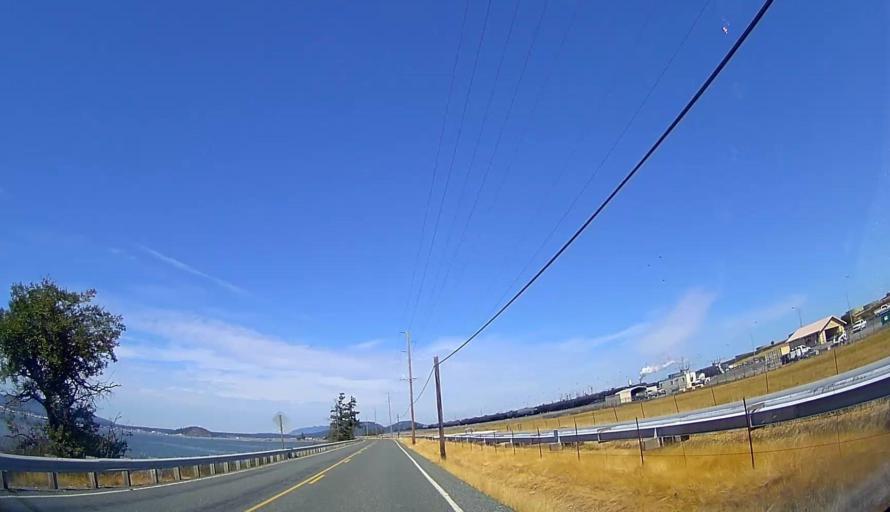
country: US
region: Washington
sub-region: Skagit County
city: Anacortes
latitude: 48.4797
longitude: -122.5732
